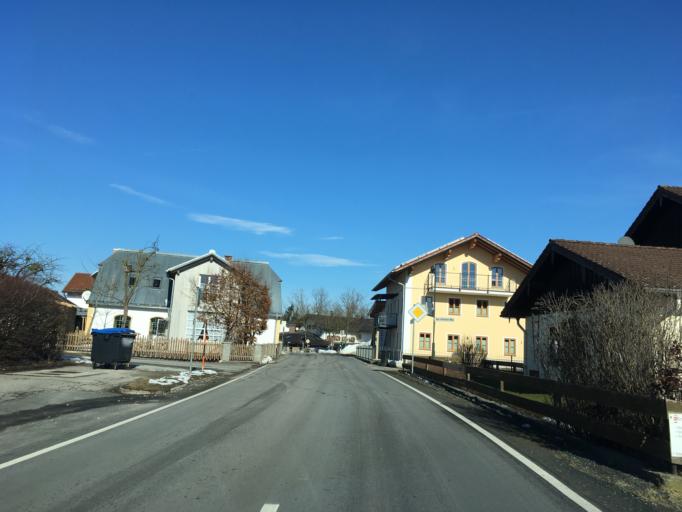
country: DE
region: Bavaria
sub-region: Upper Bavaria
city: Ramerberg
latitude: 48.0251
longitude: 12.1419
